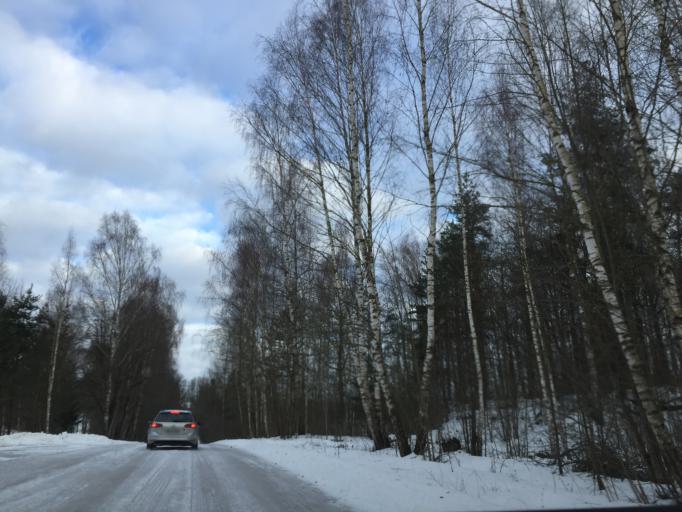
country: LV
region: Lielvarde
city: Lielvarde
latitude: 56.5738
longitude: 24.7349
